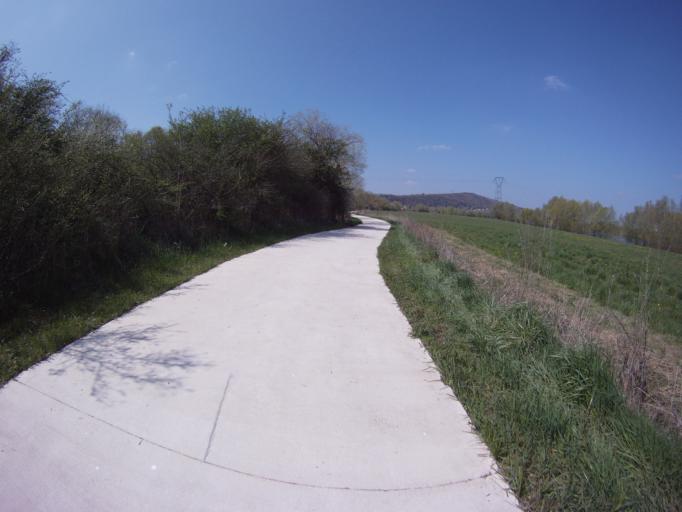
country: FR
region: Lorraine
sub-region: Departement de Meurthe-et-Moselle
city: Dieulouard
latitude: 48.8421
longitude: 6.0872
